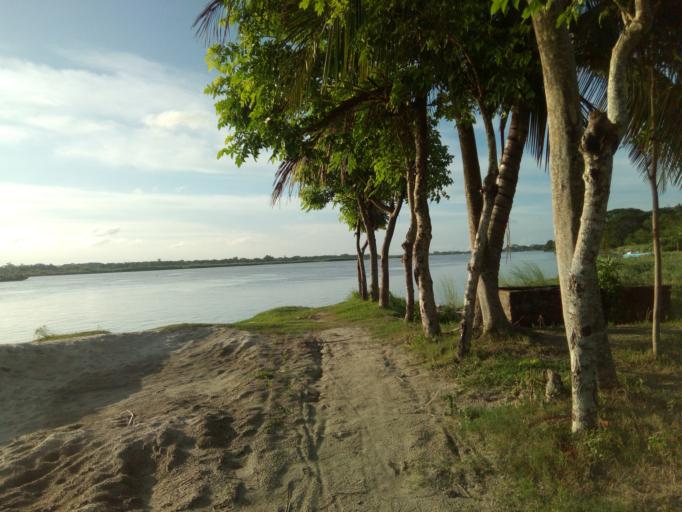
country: BD
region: Khulna
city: Kalia
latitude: 23.0451
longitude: 89.6276
